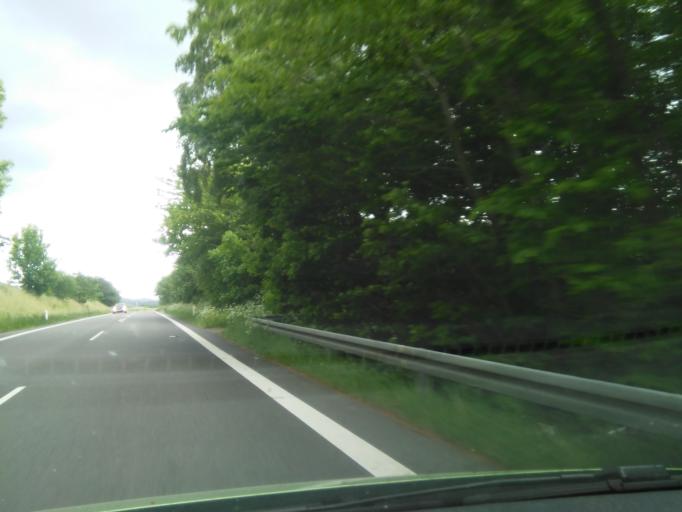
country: DK
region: Capital Region
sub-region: Bornholm Kommune
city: Akirkeby
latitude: 55.2178
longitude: 14.9202
